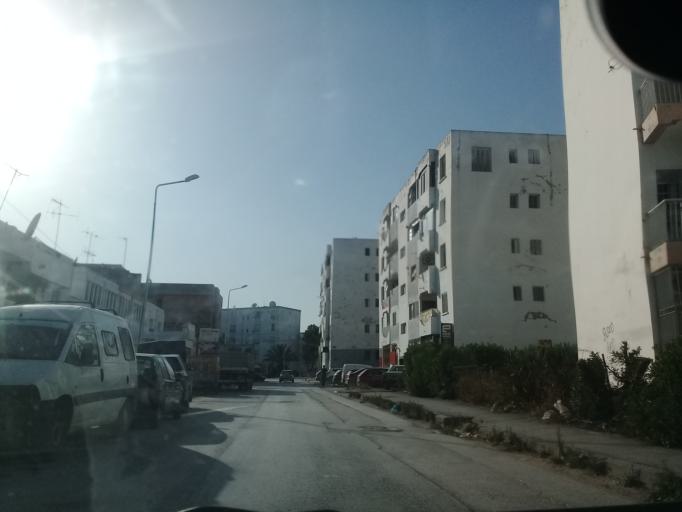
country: TN
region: Ariana
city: Ariana
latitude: 36.8351
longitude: 10.1933
